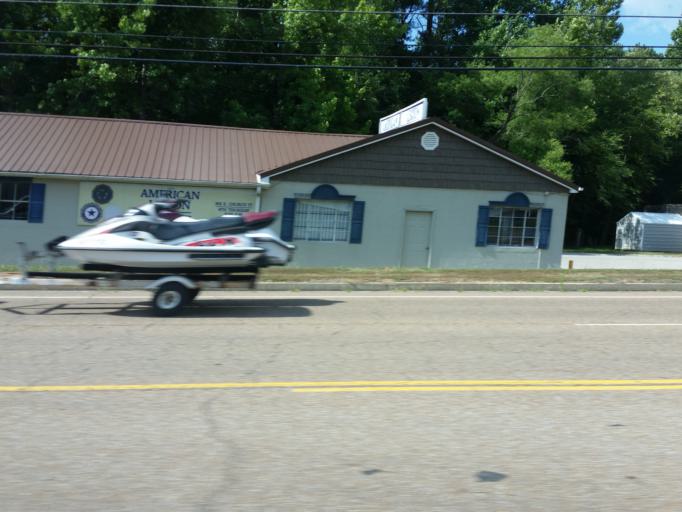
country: US
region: Tennessee
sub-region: Henderson County
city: Lexington
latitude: 35.6403
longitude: -88.3682
